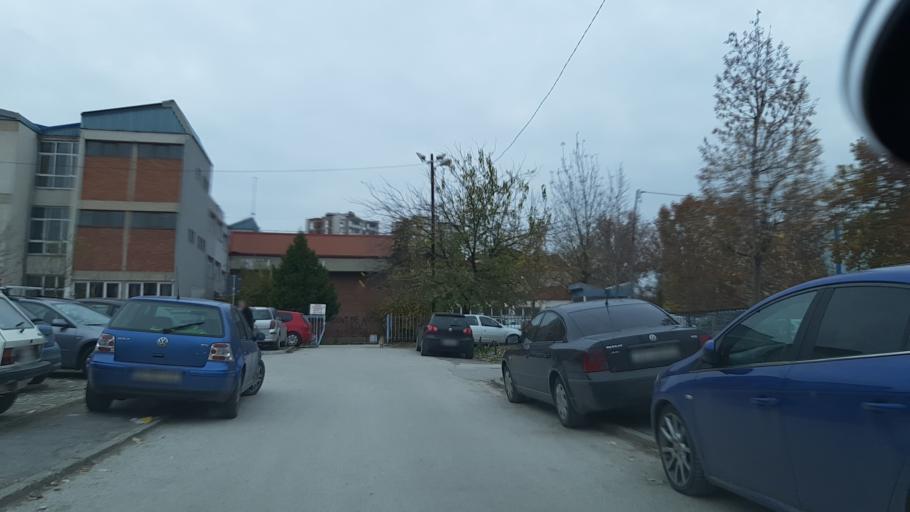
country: MK
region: Karpos
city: Skopje
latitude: 41.9899
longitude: 21.4386
